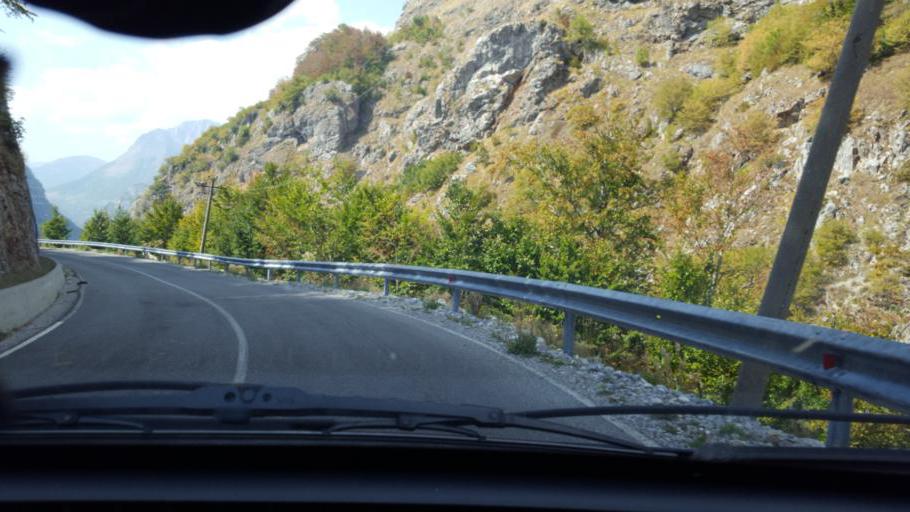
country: ME
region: Andrijevica
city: Andrijevica
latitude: 42.5370
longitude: 19.6841
